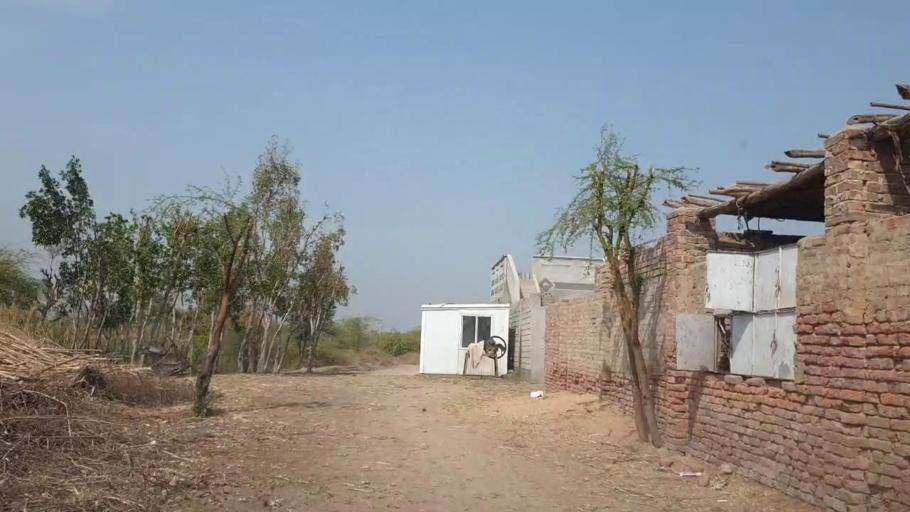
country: PK
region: Sindh
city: Mirpur Khas
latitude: 25.5530
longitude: 69.0749
